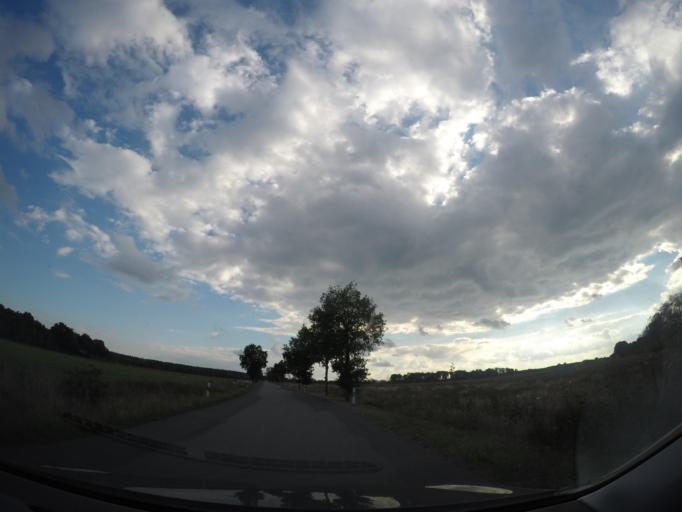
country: DE
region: Saxony-Anhalt
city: Mieste
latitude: 52.5287
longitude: 11.1504
